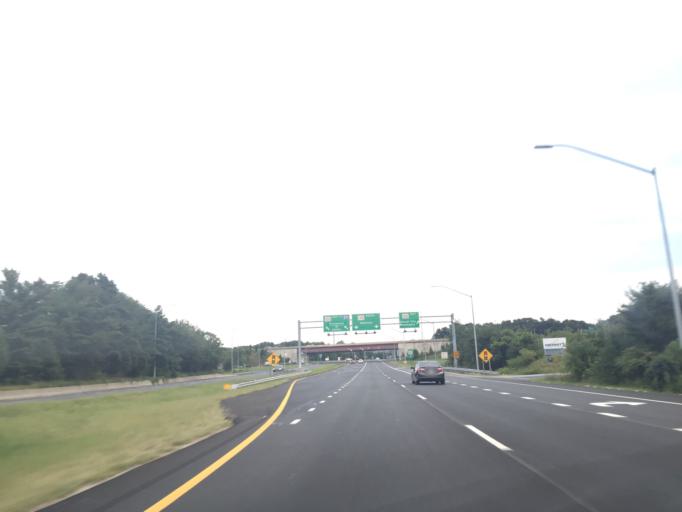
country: US
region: Maryland
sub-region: Anne Arundel County
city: Severn
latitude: 39.1511
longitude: -76.6902
